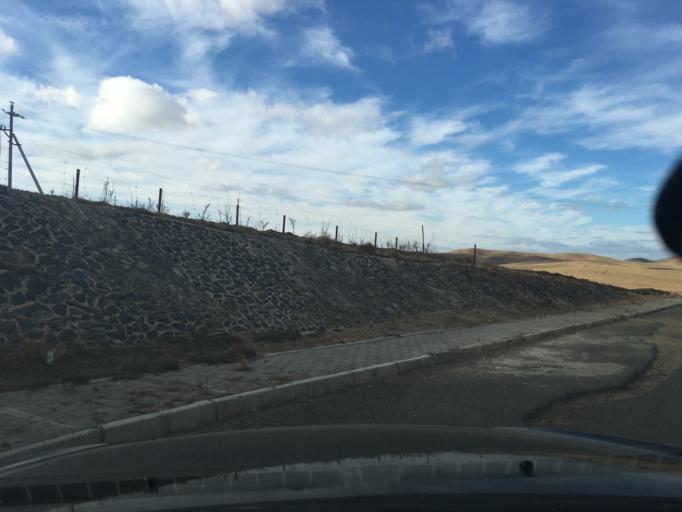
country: MN
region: Ulaanbaatar
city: Ulaanbaatar
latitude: 47.7894
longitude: 106.7451
